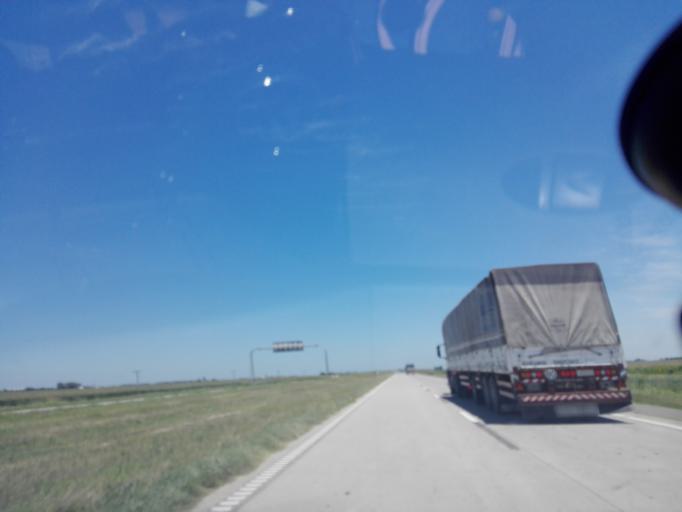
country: AR
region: Cordoba
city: Leones
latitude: -32.6361
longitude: -62.2562
